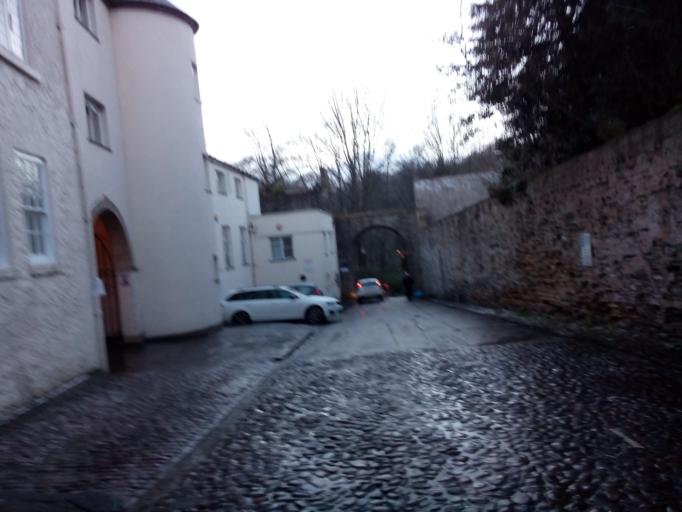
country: GB
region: England
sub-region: County Durham
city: Durham
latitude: 54.7709
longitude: -1.5773
